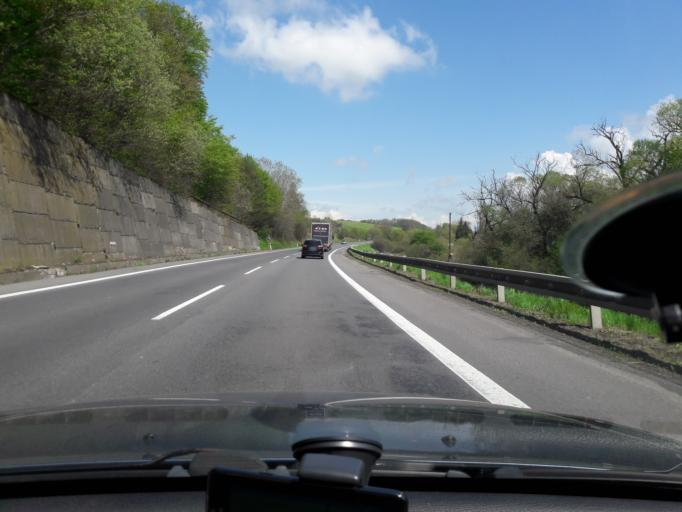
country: SK
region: Banskobystricky
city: Krupina
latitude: 48.4095
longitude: 19.0857
